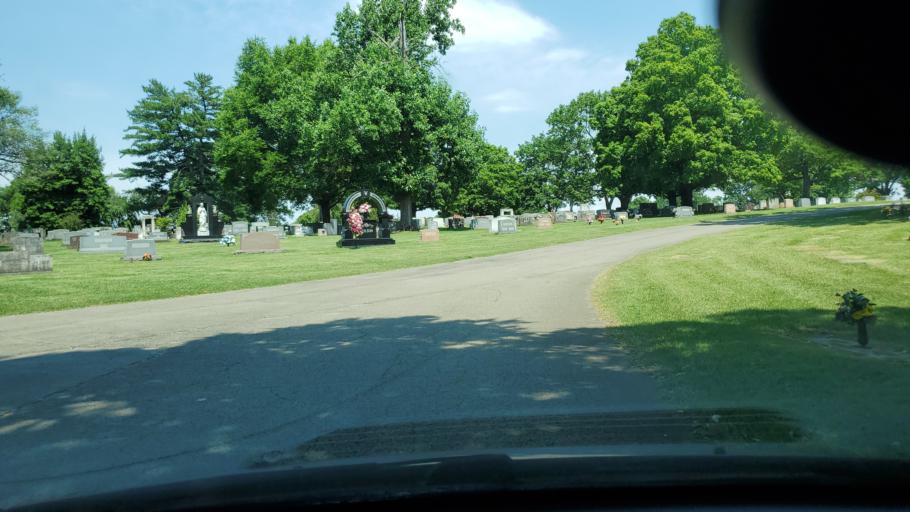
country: US
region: Tennessee
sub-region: Davidson County
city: Goodlettsville
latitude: 36.2407
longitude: -86.7209
